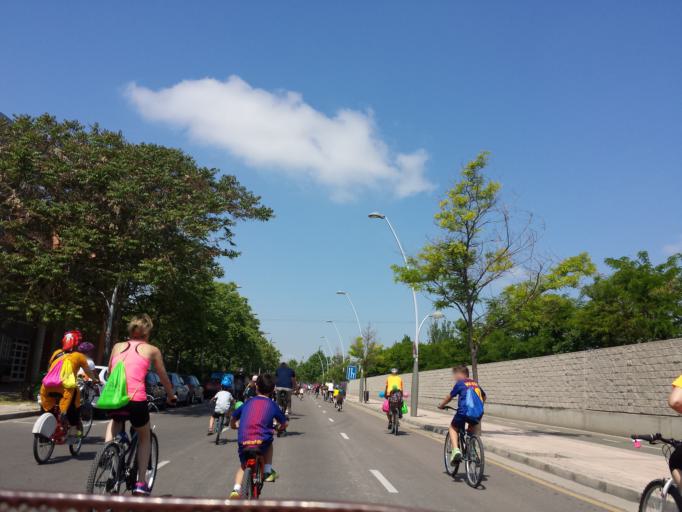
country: ES
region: Aragon
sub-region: Provincia de Zaragoza
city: Almozara
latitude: 41.6641
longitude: -0.9030
